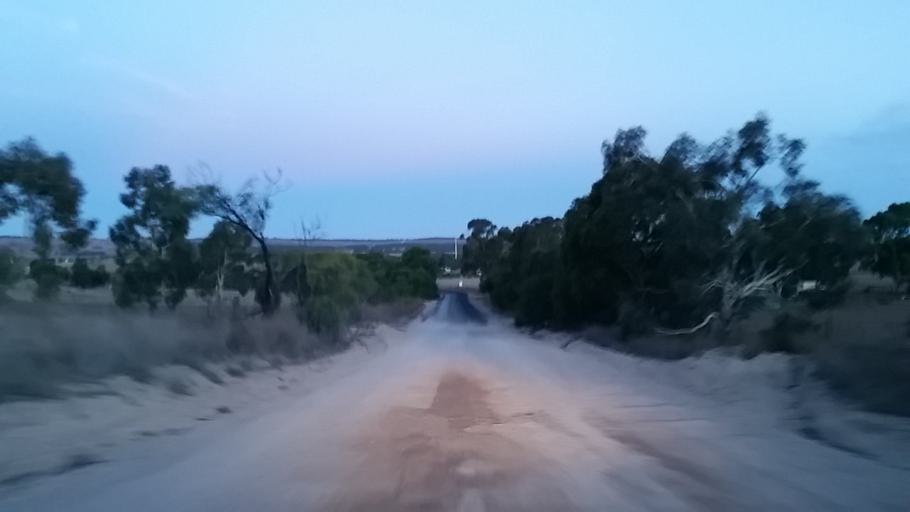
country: AU
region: South Australia
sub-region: Mount Barker
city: Callington
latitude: -35.1074
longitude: 139.0253
